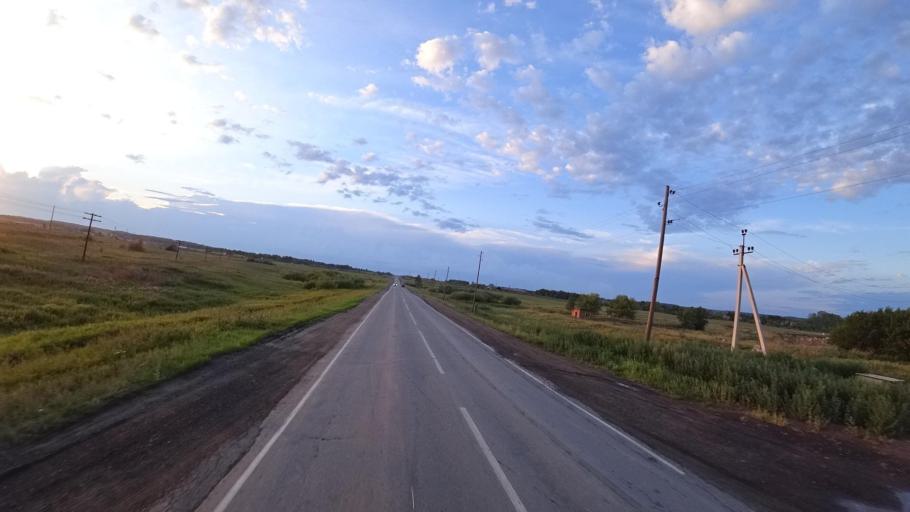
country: RU
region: Sverdlovsk
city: Kamyshlov
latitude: 56.8702
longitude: 62.7111
